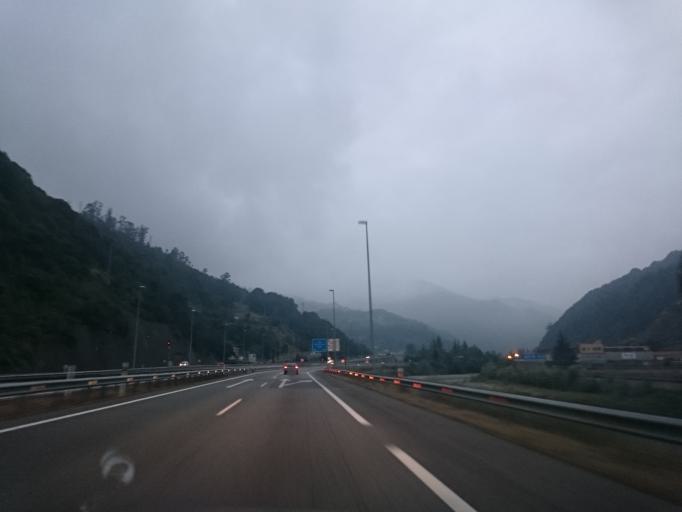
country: ES
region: Asturias
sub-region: Province of Asturias
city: Mieres
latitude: 43.2056
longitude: -5.7875
